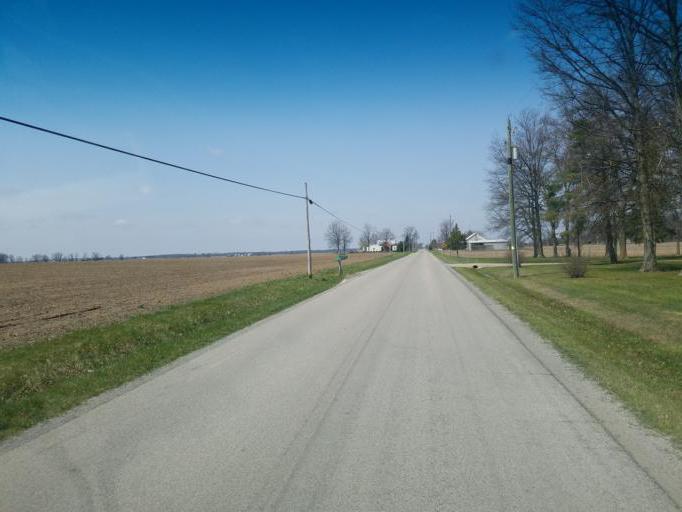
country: US
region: Ohio
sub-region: Wyandot County
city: Upper Sandusky
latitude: 40.8764
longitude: -83.2836
